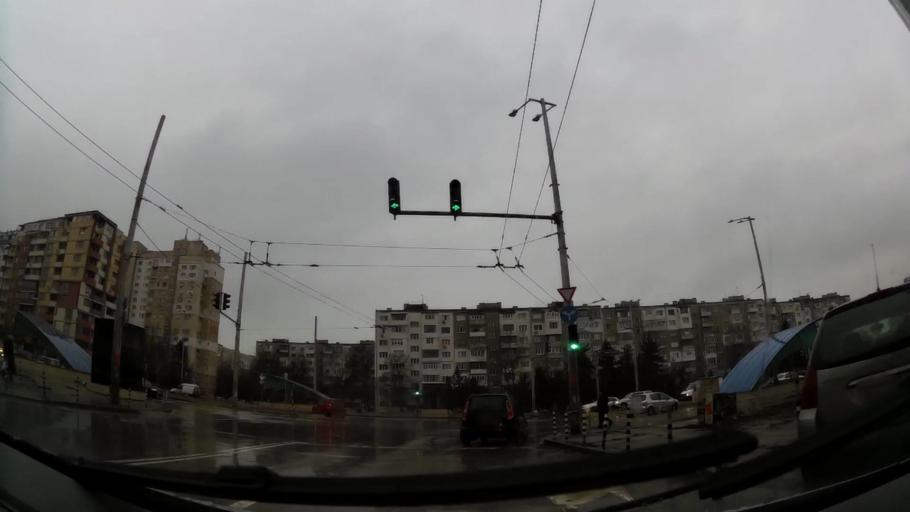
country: BG
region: Sofia-Capital
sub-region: Stolichna Obshtina
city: Sofia
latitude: 42.6541
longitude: 23.3723
